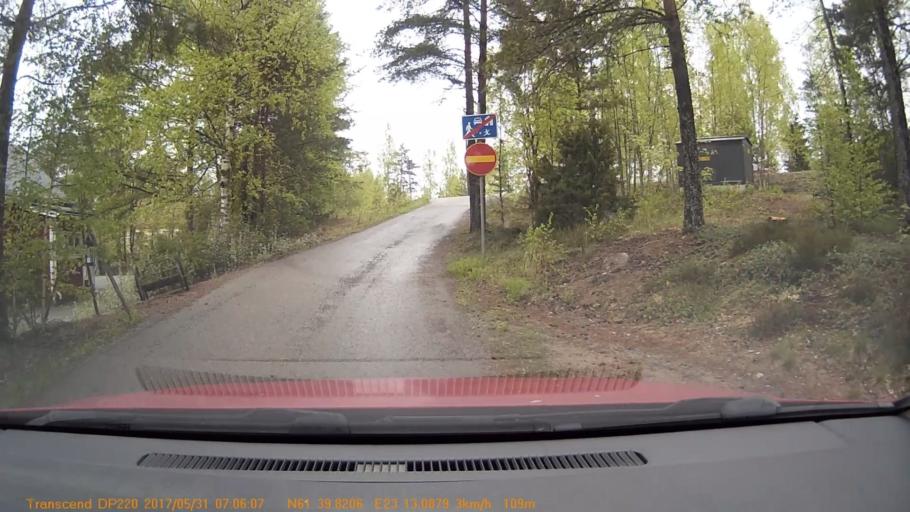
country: FI
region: Pirkanmaa
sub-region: Tampere
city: Haemeenkyroe
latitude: 61.6636
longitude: 23.2182
